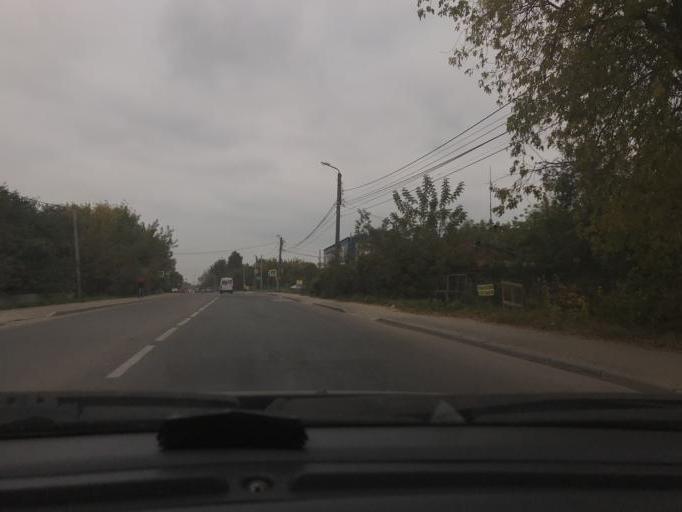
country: RU
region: Kaluga
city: Kaluga
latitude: 54.5151
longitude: 36.3373
